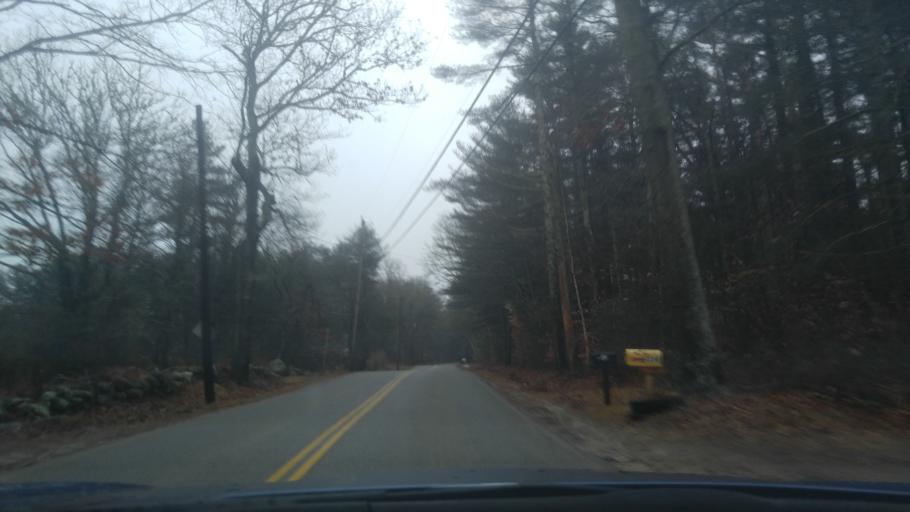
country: US
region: Rhode Island
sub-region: Washington County
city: Charlestown
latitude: 41.4436
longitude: -71.6108
